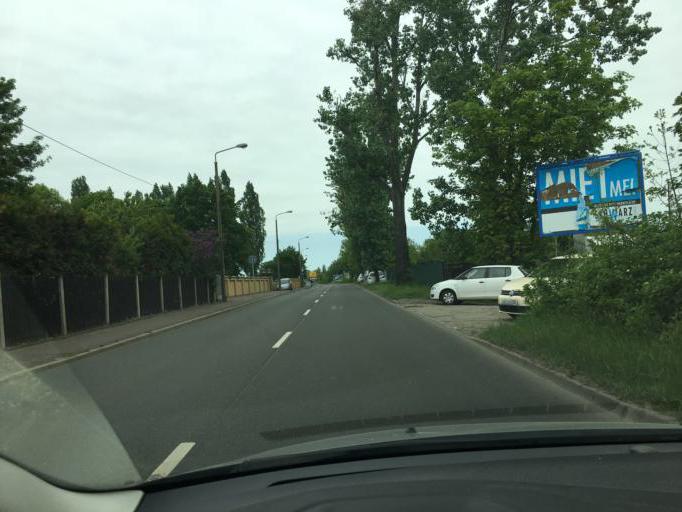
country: DE
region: Saxony
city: Taucha
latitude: 51.3548
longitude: 12.4443
